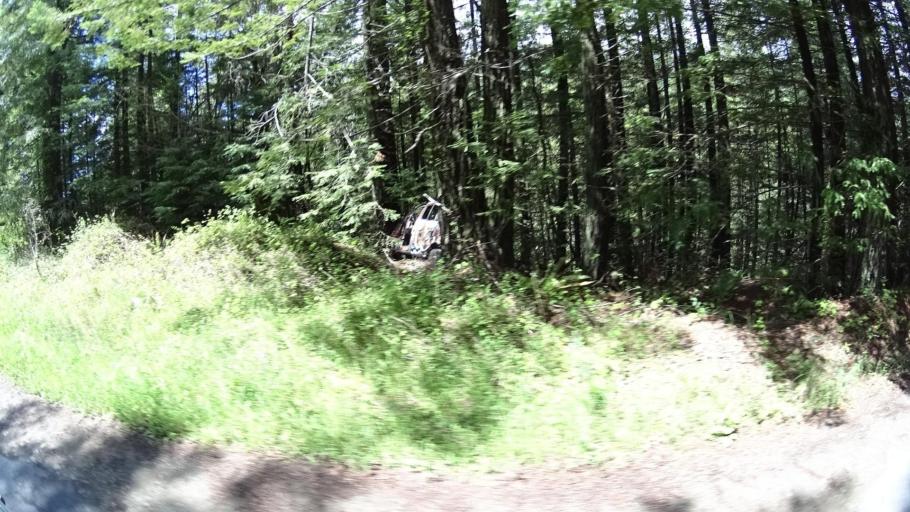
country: US
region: California
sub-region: Humboldt County
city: Blue Lake
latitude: 40.8421
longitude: -123.8951
